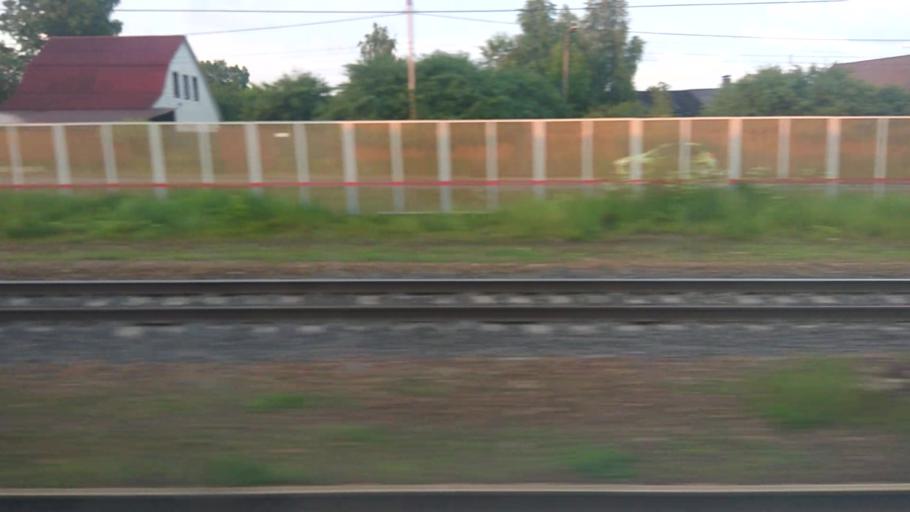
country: RU
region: Moskovskaya
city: Barybino
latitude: 55.2716
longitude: 37.8955
